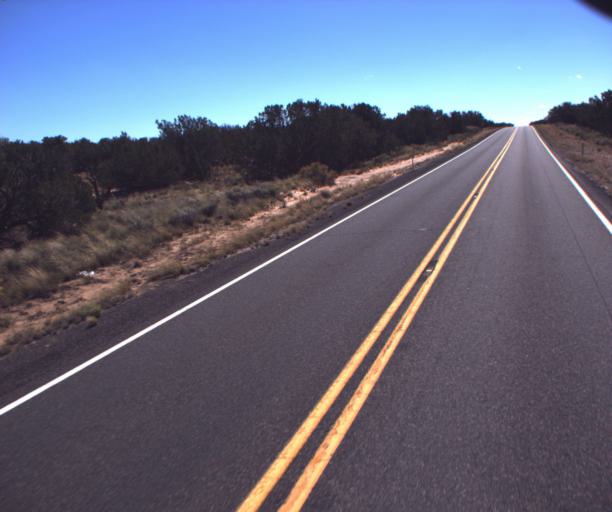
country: US
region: Arizona
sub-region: Apache County
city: Saint Johns
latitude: 34.8489
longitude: -109.2377
